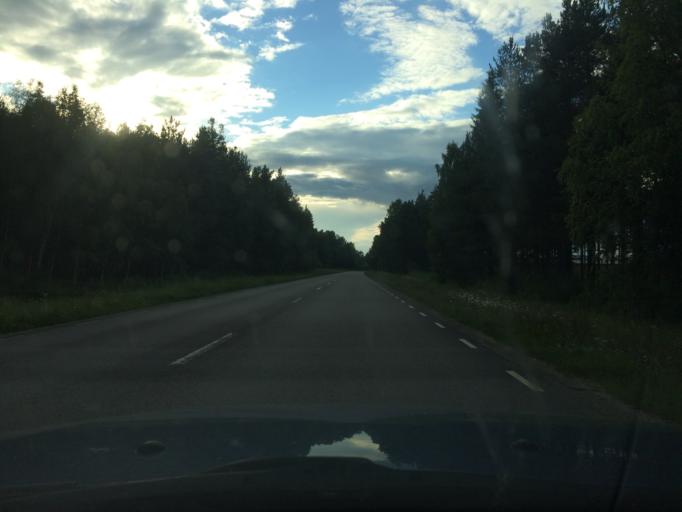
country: SE
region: Norrbotten
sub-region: Pitea Kommun
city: Bergsviken
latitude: 65.3334
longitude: 21.4185
